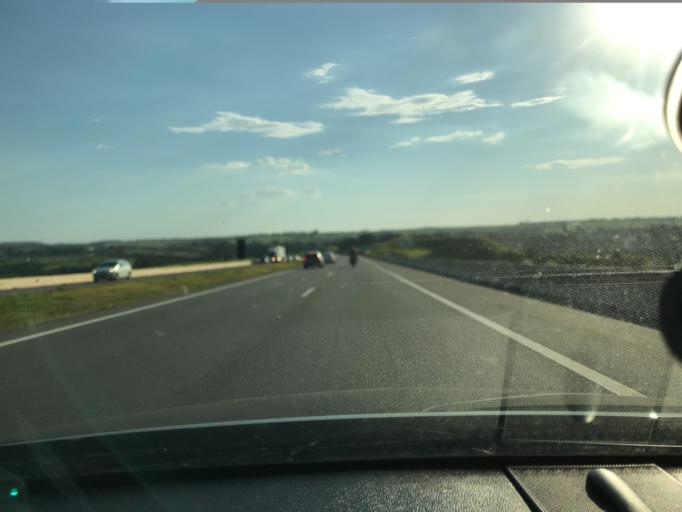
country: BR
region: Sao Paulo
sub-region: Valinhos
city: Valinhos
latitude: -22.9989
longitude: -47.0776
